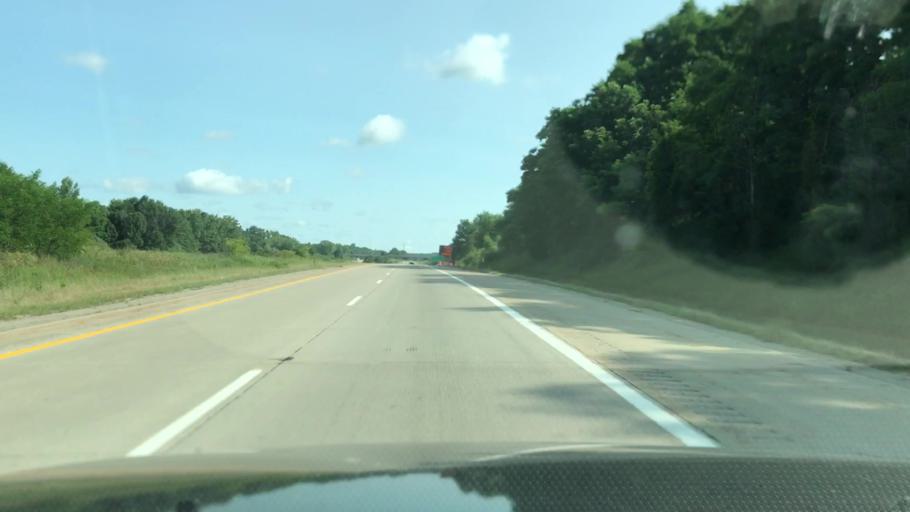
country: US
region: Michigan
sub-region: Kent County
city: Northview
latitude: 43.0793
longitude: -85.6377
